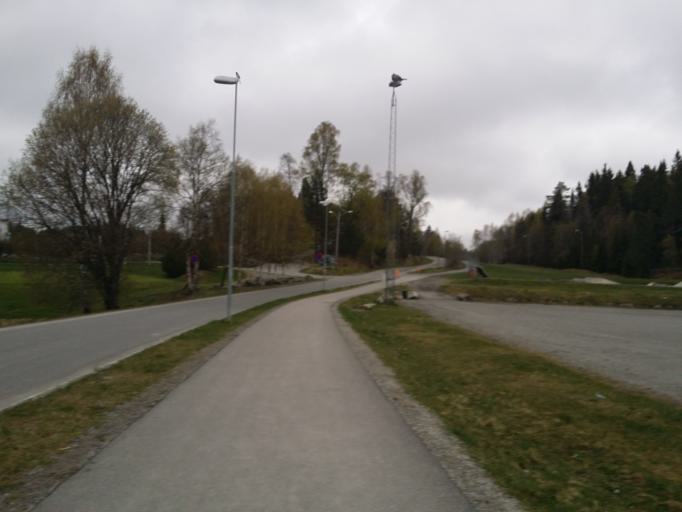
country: NO
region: Akershus
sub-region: Oppegard
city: Kolbotn
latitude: 59.7748
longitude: 10.8150
